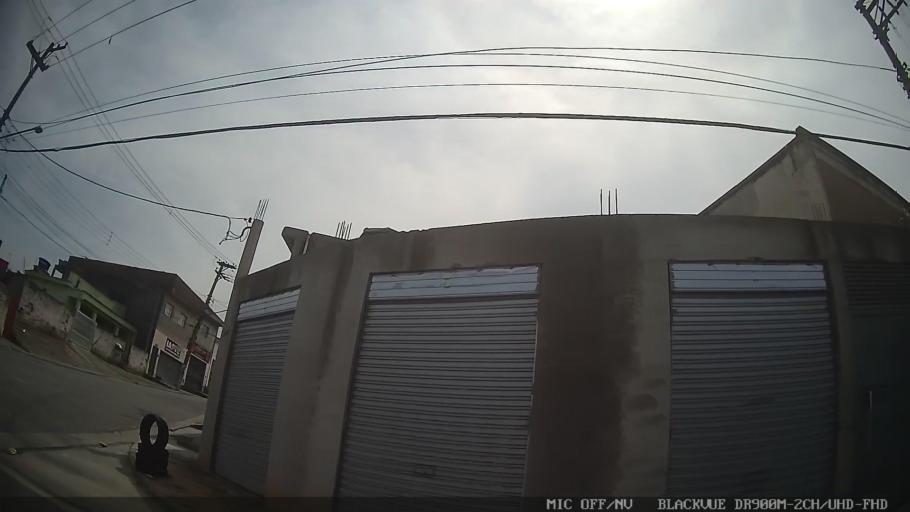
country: BR
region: Sao Paulo
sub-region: Ferraz De Vasconcelos
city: Ferraz de Vasconcelos
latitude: -23.5506
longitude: -46.3942
